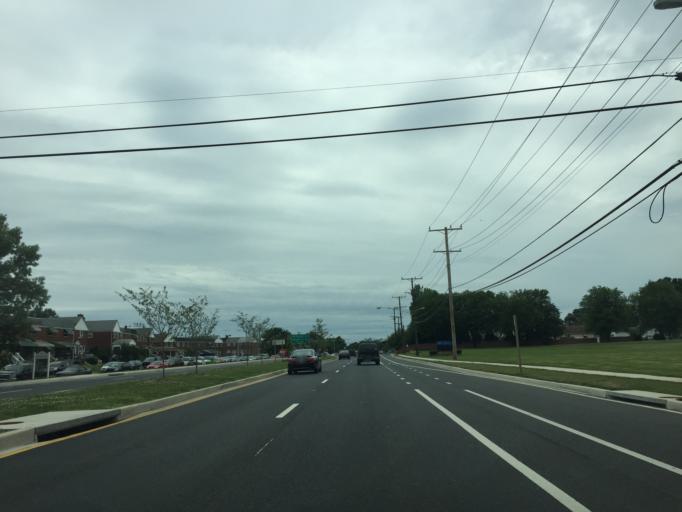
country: US
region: Maryland
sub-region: Baltimore County
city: Dundalk
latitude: 39.2660
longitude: -76.5057
